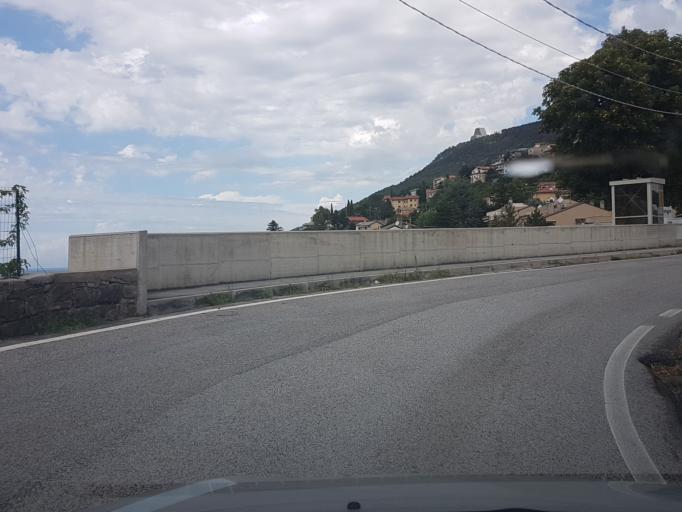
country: IT
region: Friuli Venezia Giulia
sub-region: Provincia di Trieste
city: Villa Opicina
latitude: 45.6794
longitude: 13.7607
